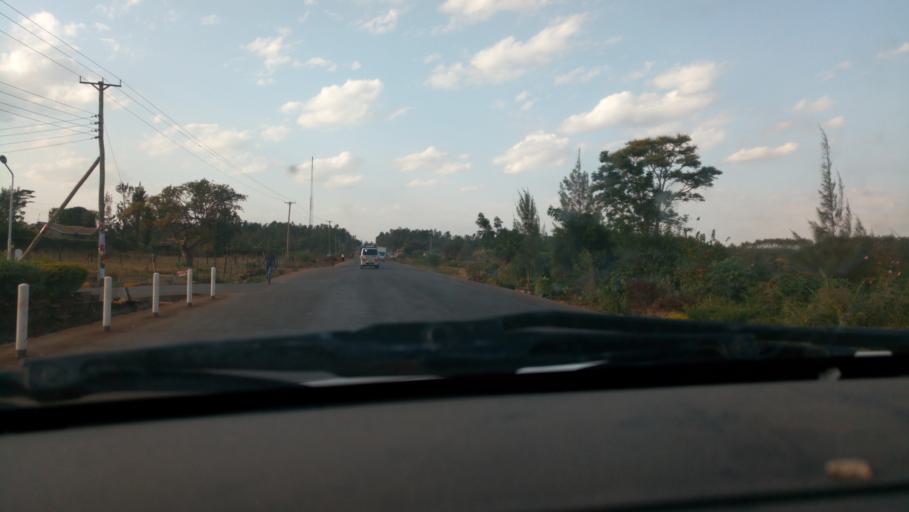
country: KE
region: Murang'a District
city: Maragua
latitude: -0.8414
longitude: 37.1383
